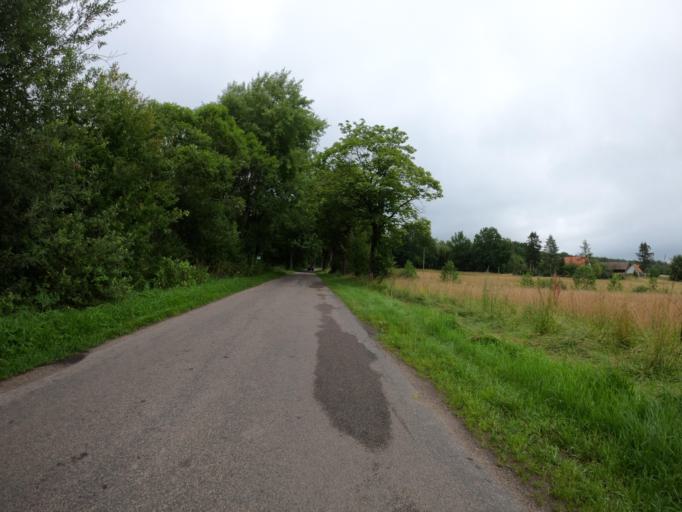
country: PL
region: West Pomeranian Voivodeship
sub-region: Powiat szczecinecki
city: Grzmiaca
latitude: 53.9046
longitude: 16.5000
